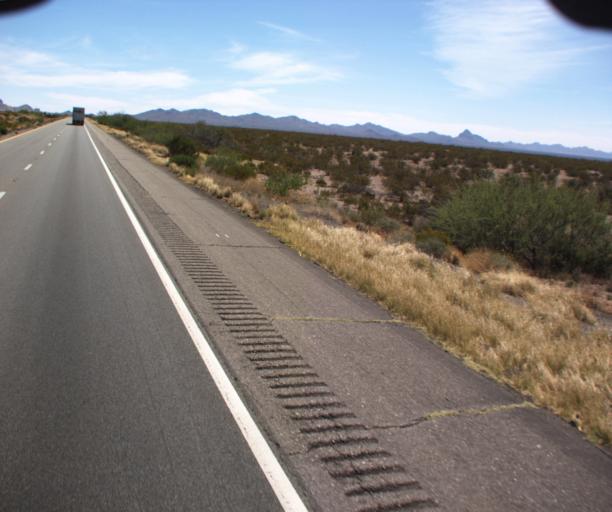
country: US
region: New Mexico
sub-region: Hidalgo County
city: Lordsburg
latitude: 32.2460
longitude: -109.1296
